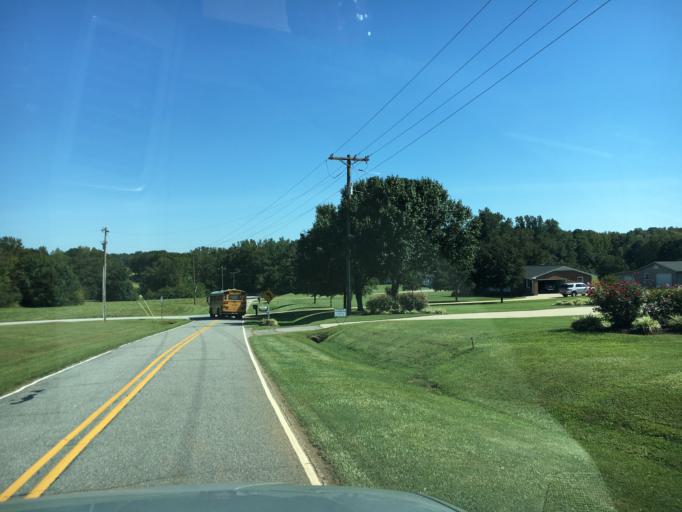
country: US
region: South Carolina
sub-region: Spartanburg County
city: Duncan
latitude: 34.8603
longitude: -82.1696
